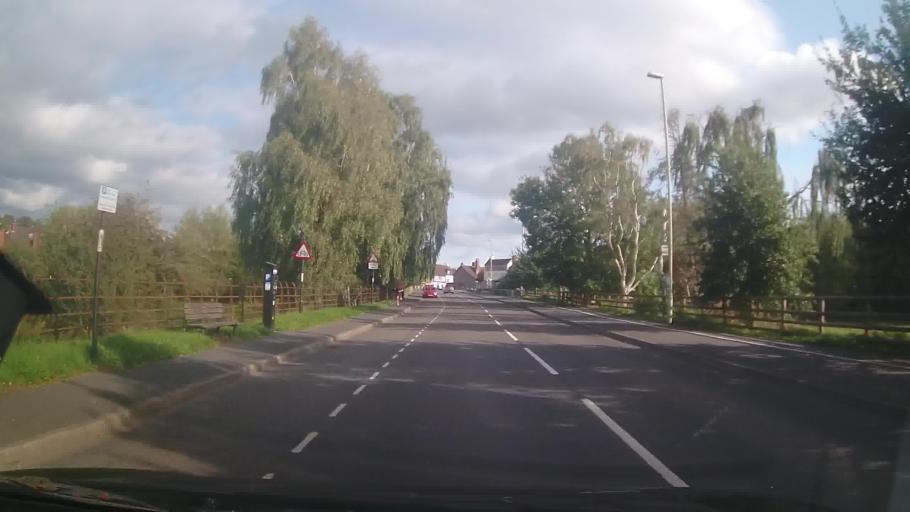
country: GB
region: England
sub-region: Shropshire
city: Ludlow
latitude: 52.3735
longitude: -2.7216
